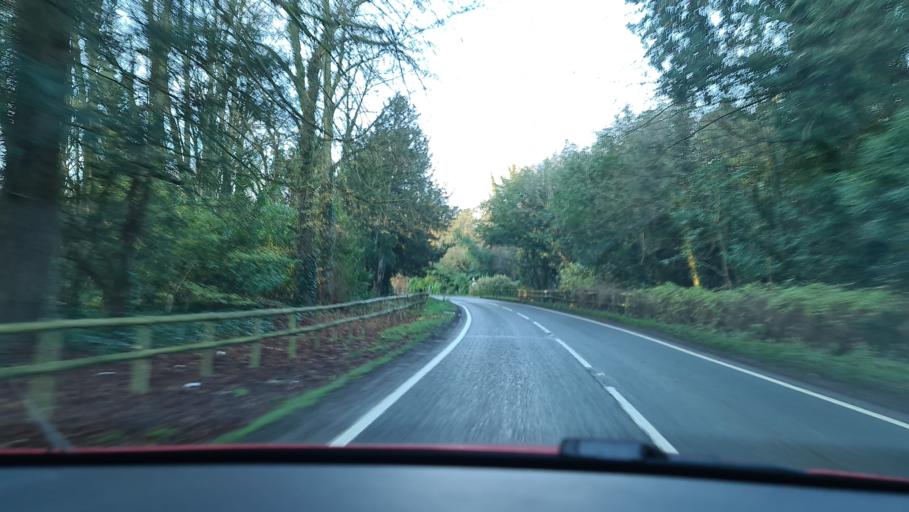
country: GB
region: England
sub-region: Buckinghamshire
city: Waddesdon
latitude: 51.8285
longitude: -0.9097
